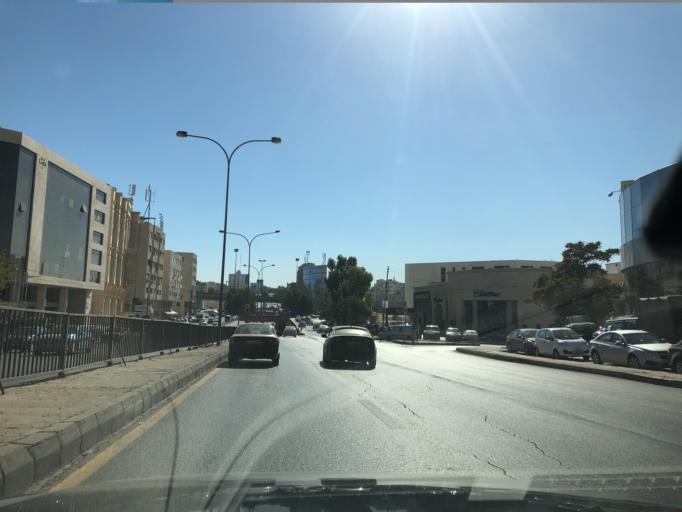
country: JO
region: Amman
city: Wadi as Sir
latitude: 31.9752
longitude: 35.8623
